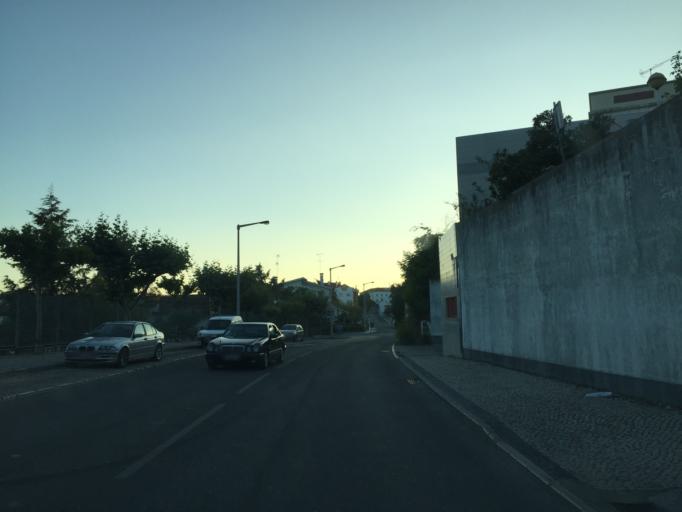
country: PT
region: Santarem
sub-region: Ourem
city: Ourem
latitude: 39.6561
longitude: -8.5706
